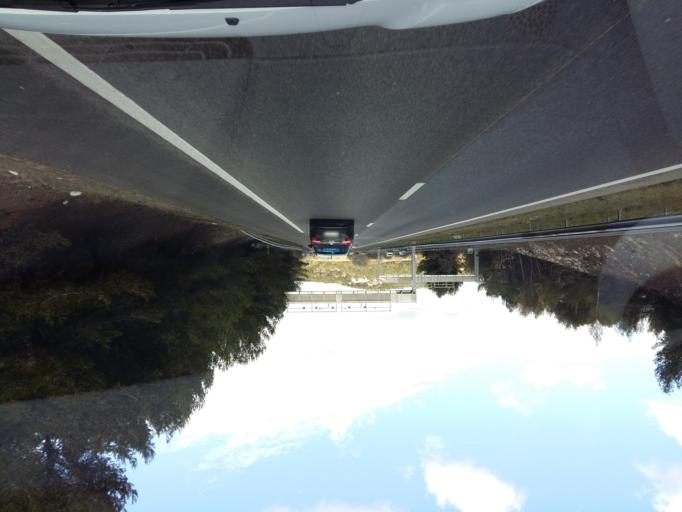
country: FR
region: Provence-Alpes-Cote d'Azur
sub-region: Departement des Bouches-du-Rhone
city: Cabries
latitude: 43.4457
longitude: 5.3961
